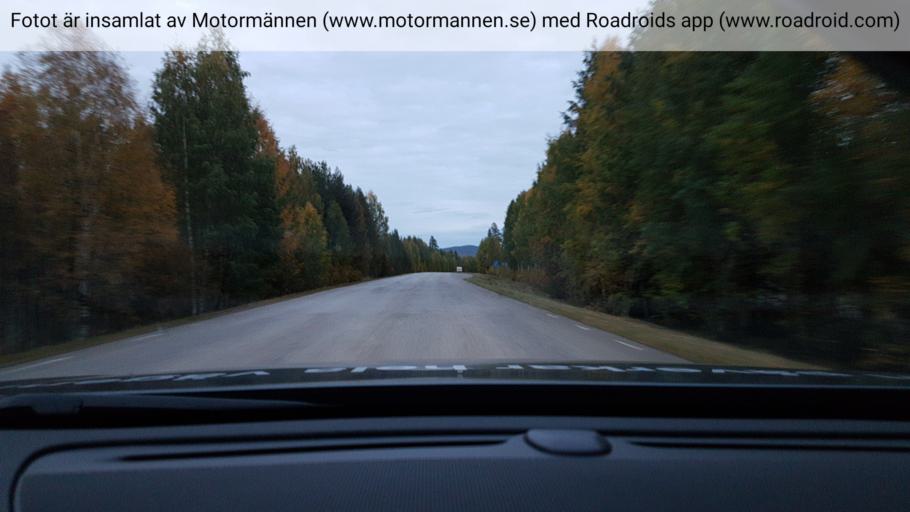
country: SE
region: Norrbotten
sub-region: Alvsbyns Kommun
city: AElvsbyn
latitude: 65.8444
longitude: 20.4821
